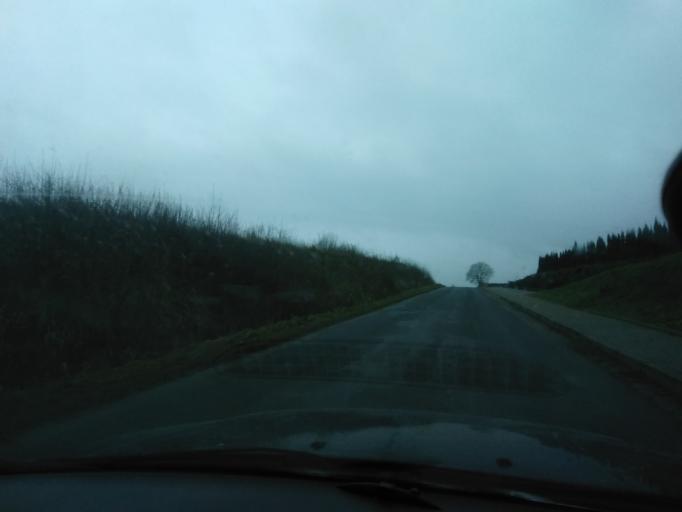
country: PL
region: Subcarpathian Voivodeship
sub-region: Powiat jaroslawski
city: Rokietnica
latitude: 49.9130
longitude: 22.6116
